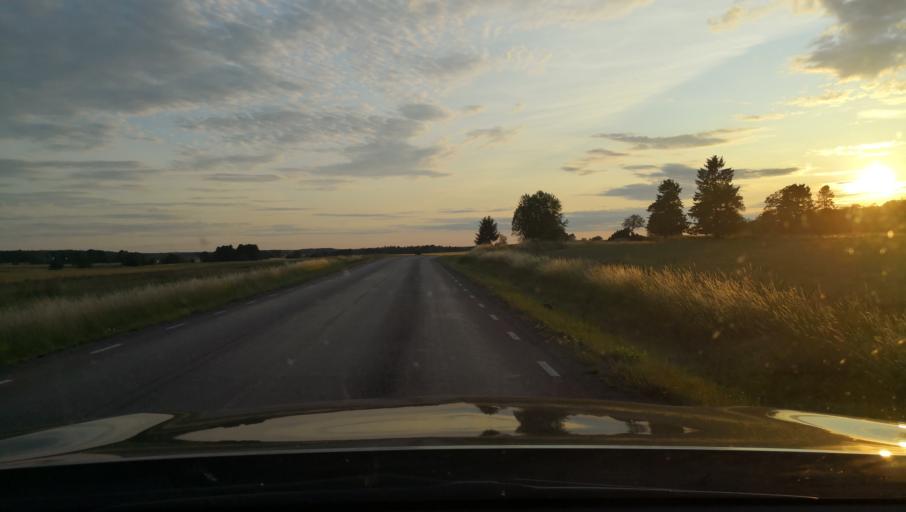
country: SE
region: Uppsala
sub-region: Uppsala Kommun
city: Vattholma
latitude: 60.0180
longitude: 17.7091
